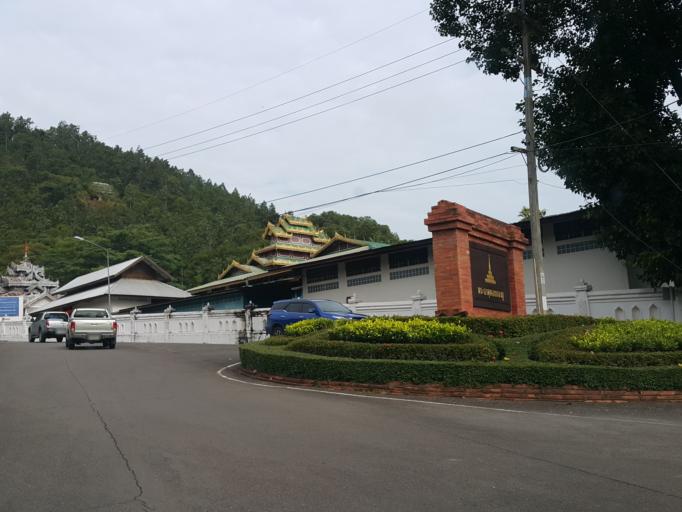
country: TH
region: Mae Hong Son
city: Mae Hong Son
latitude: 19.2978
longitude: 97.9635
